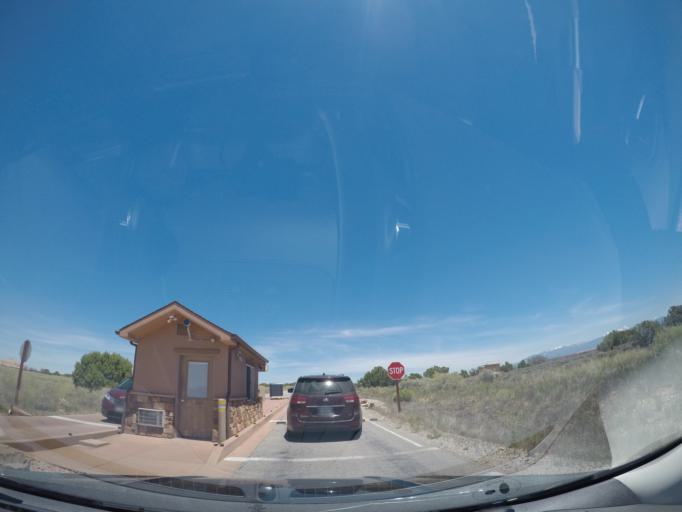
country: US
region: Utah
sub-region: Grand County
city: Moab
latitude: 38.4733
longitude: -109.8096
